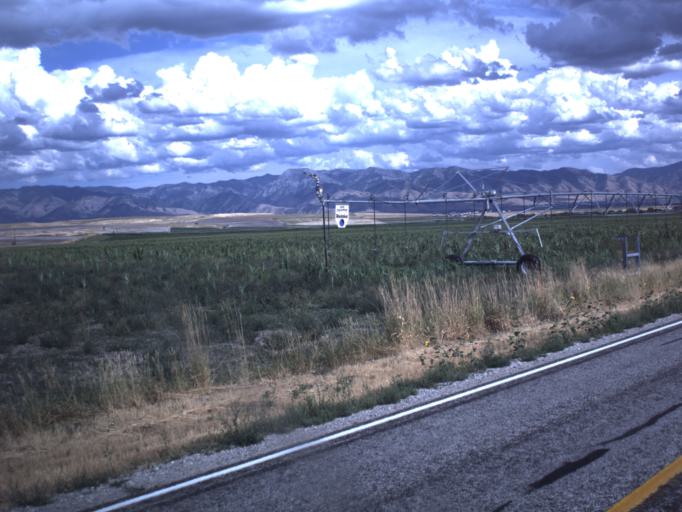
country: US
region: Utah
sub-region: Cache County
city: Benson
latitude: 41.8729
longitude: -112.0168
